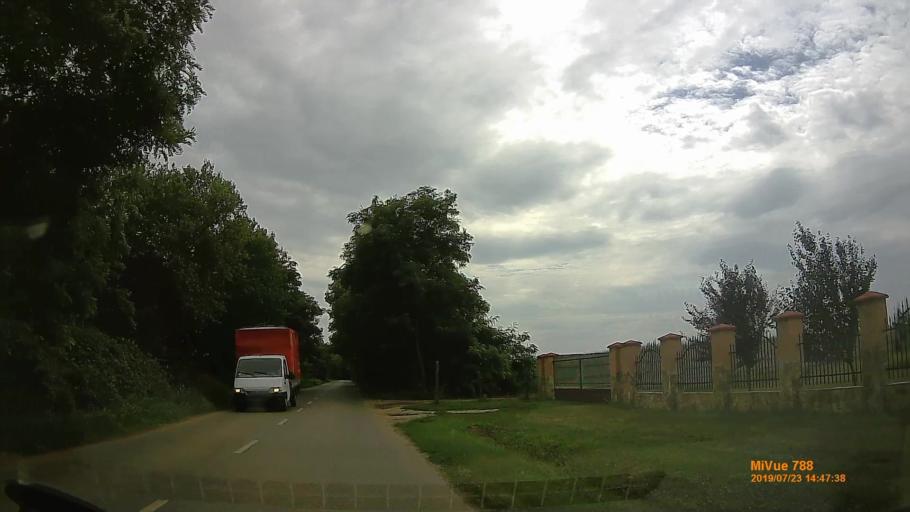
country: HU
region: Szabolcs-Szatmar-Bereg
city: Nyiregyhaza
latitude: 47.9098
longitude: 21.6740
